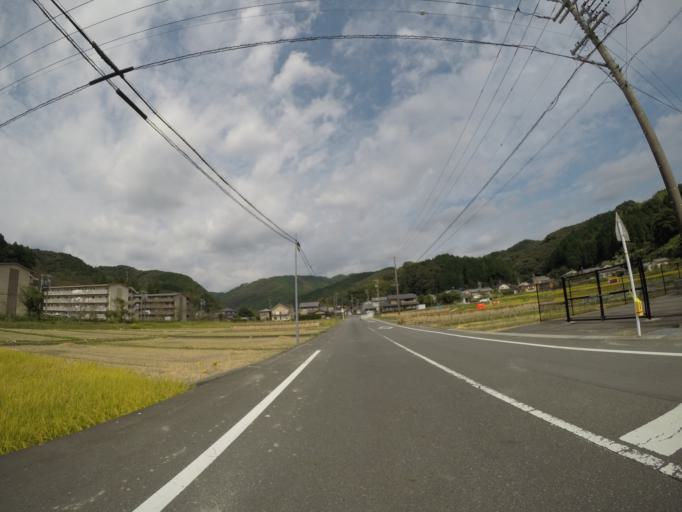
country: JP
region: Shizuoka
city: Shimada
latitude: 34.8648
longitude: 138.1833
